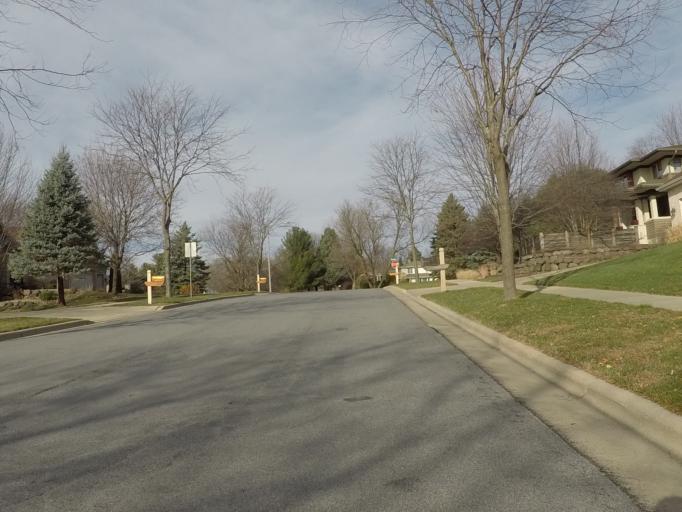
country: US
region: Wisconsin
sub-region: Dane County
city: Middleton
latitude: 43.0814
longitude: -89.5403
